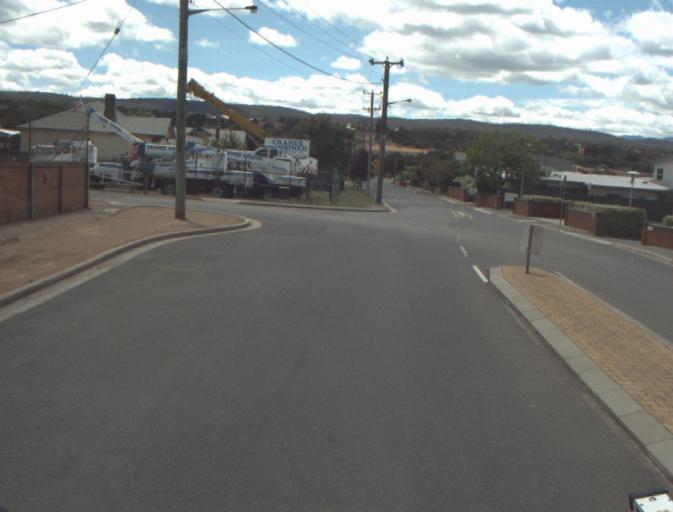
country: AU
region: Tasmania
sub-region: Launceston
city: East Launceston
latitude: -41.4320
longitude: 147.1573
